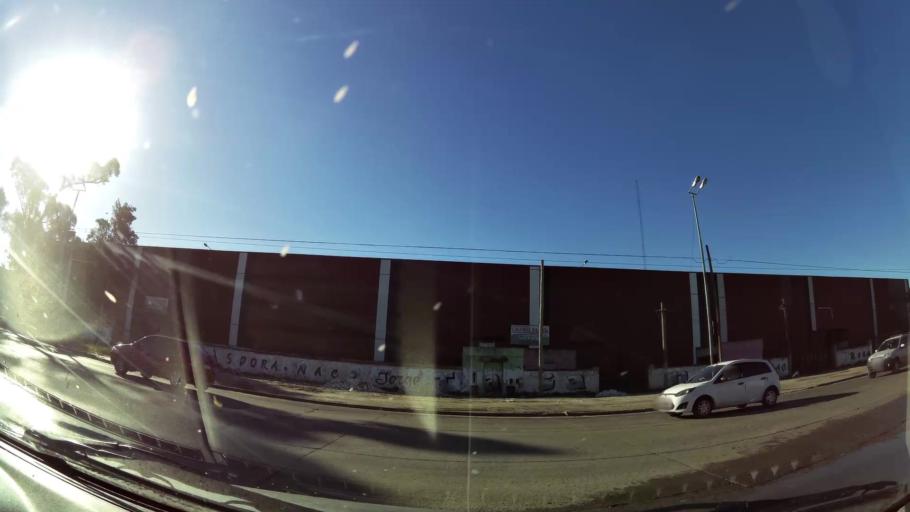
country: AR
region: Buenos Aires
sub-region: Partido de Quilmes
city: Quilmes
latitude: -34.7408
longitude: -58.3214
